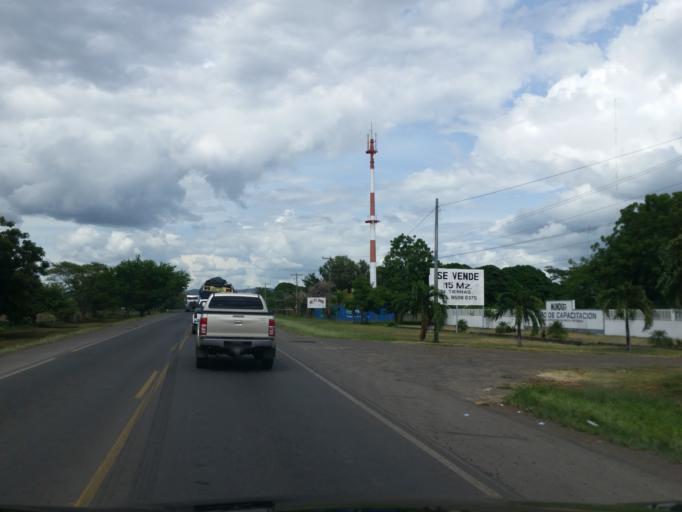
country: NI
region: Managua
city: Tipitapa
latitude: 12.2719
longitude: -86.0720
